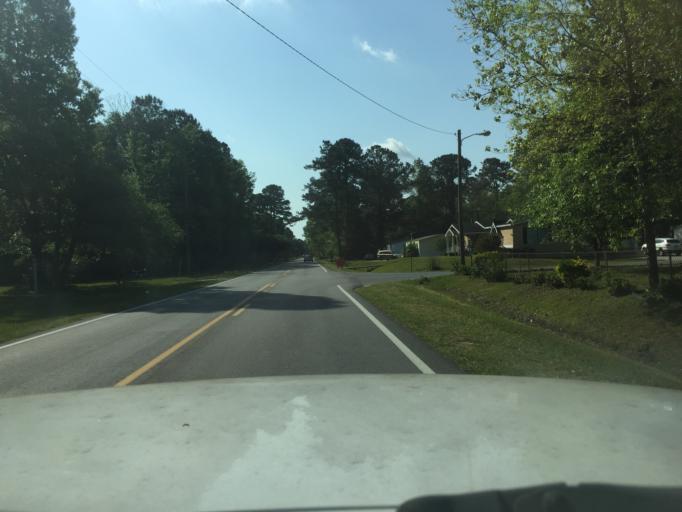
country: US
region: Georgia
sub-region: Chatham County
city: Georgetown
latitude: 32.0282
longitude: -81.2198
